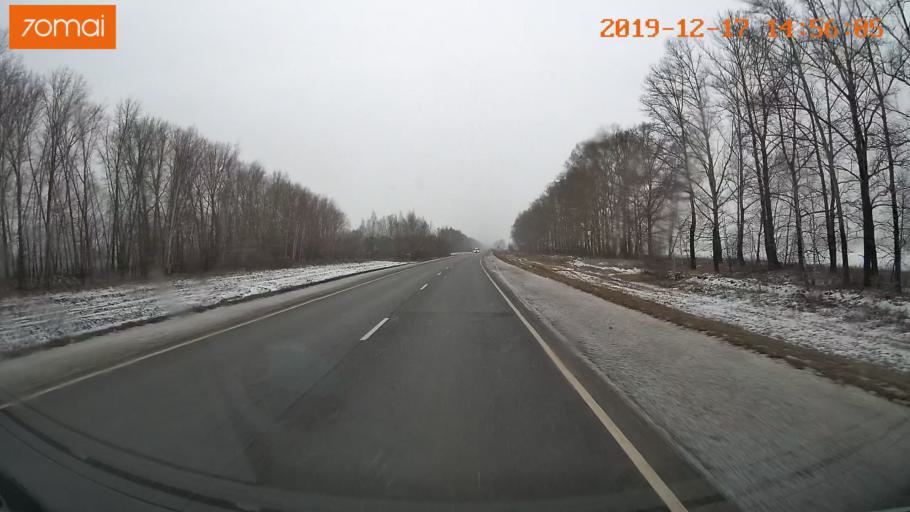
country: RU
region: Rjazan
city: Zakharovo
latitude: 54.3448
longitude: 39.2573
